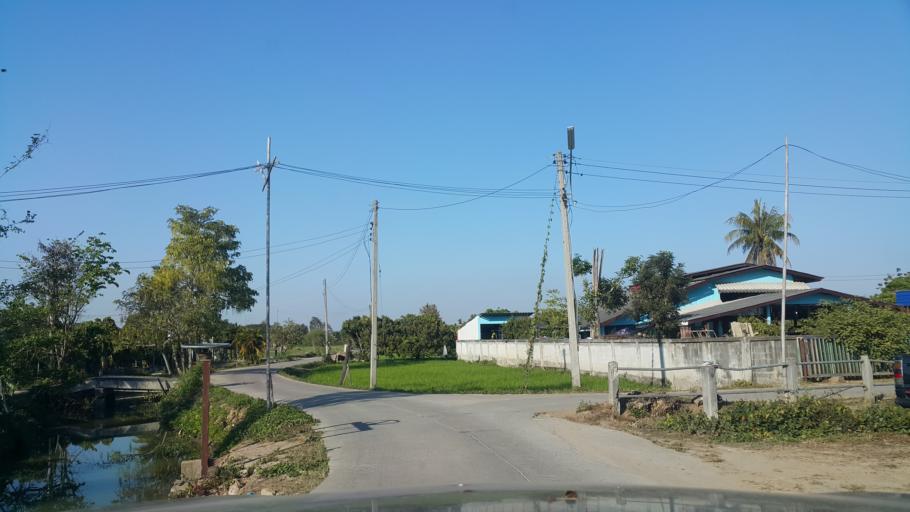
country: TH
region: Chiang Mai
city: Hang Dong
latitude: 18.6756
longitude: 98.9683
